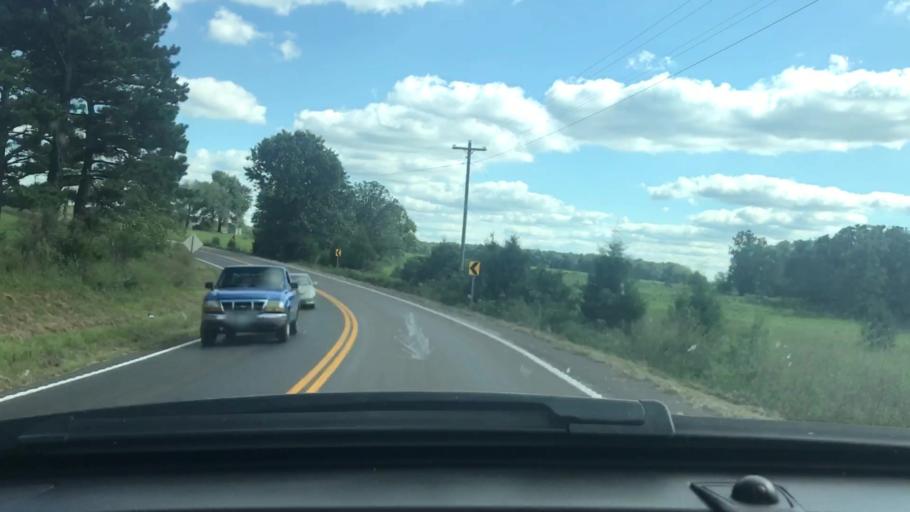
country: US
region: Missouri
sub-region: Wright County
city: Mountain Grove
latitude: 37.2349
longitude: -92.3006
